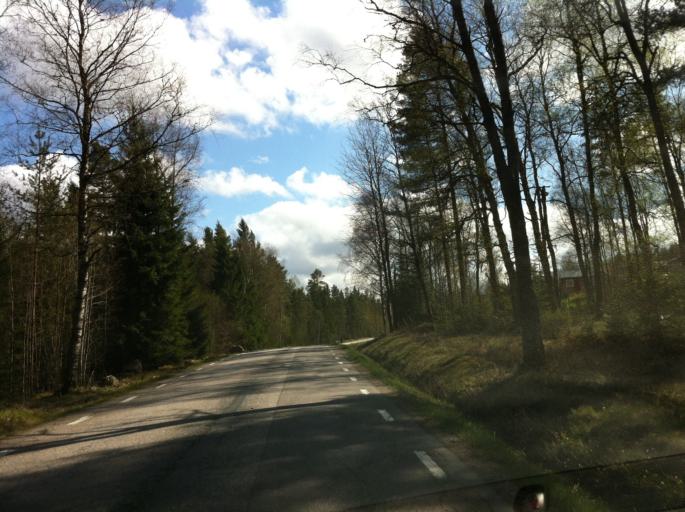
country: SE
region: Vaestra Goetaland
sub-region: Alingsas Kommun
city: Alingsas
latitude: 57.8256
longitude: 12.6457
